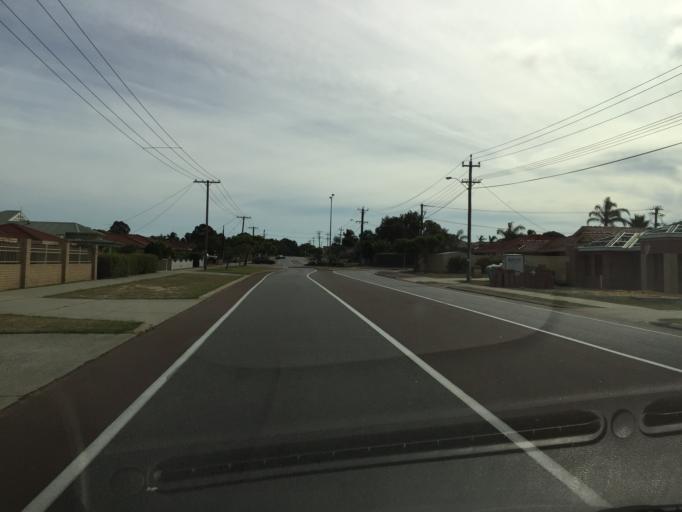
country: AU
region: Western Australia
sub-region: Canning
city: Willetton
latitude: -32.0553
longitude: 115.9011
